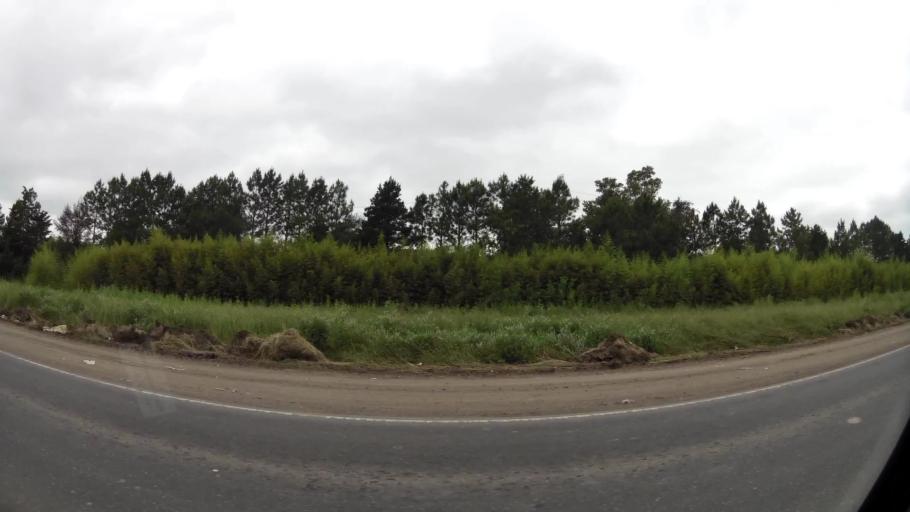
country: AR
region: Buenos Aires
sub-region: Partido de Ezeiza
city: Ezeiza
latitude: -34.8892
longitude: -58.5060
